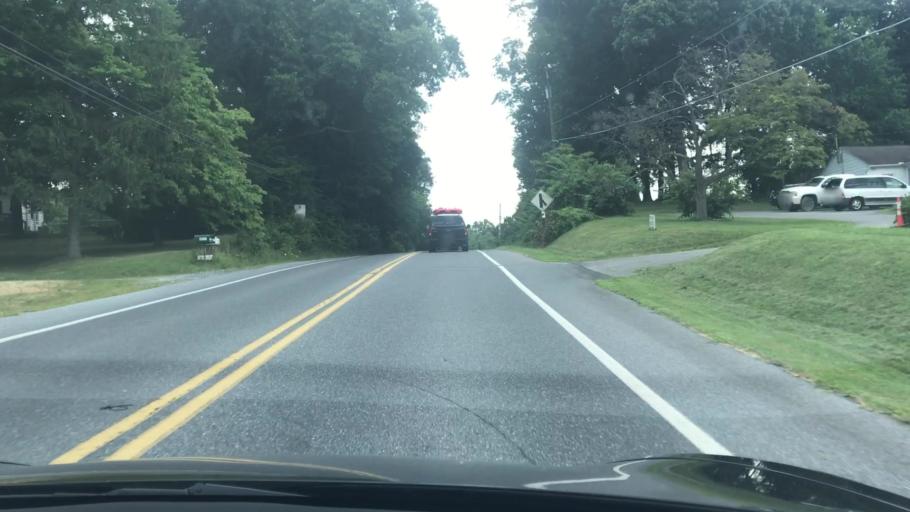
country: US
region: Pennsylvania
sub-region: York County
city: Valley Green
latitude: 40.1129
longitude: -76.7726
